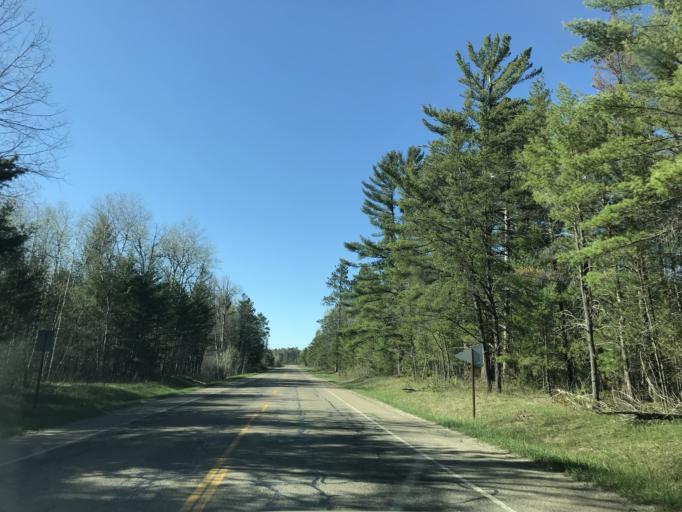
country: US
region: Michigan
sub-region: Crawford County
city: Grayling
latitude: 44.7134
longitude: -84.7429
